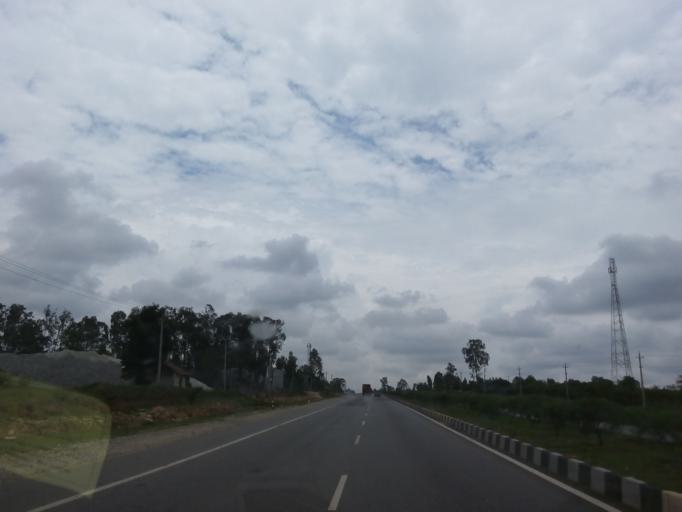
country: IN
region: Karnataka
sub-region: Hassan
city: Channarayapatna
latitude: 12.9741
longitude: 76.2776
